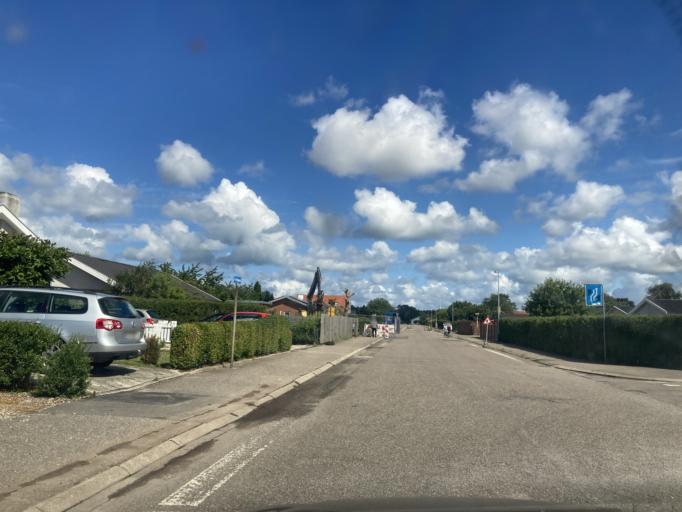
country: DK
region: Capital Region
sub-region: Halsnaes Kommune
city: Frederiksvaerk
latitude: 55.9881
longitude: 12.0101
